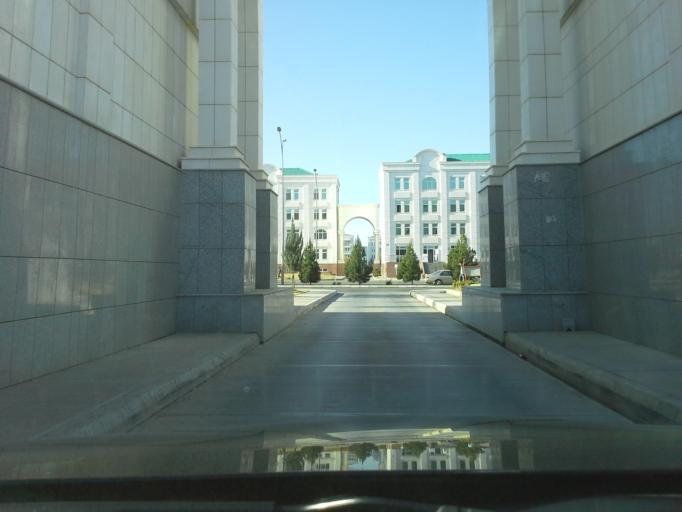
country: TM
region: Ahal
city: Ashgabat
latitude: 37.9697
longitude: 58.3351
